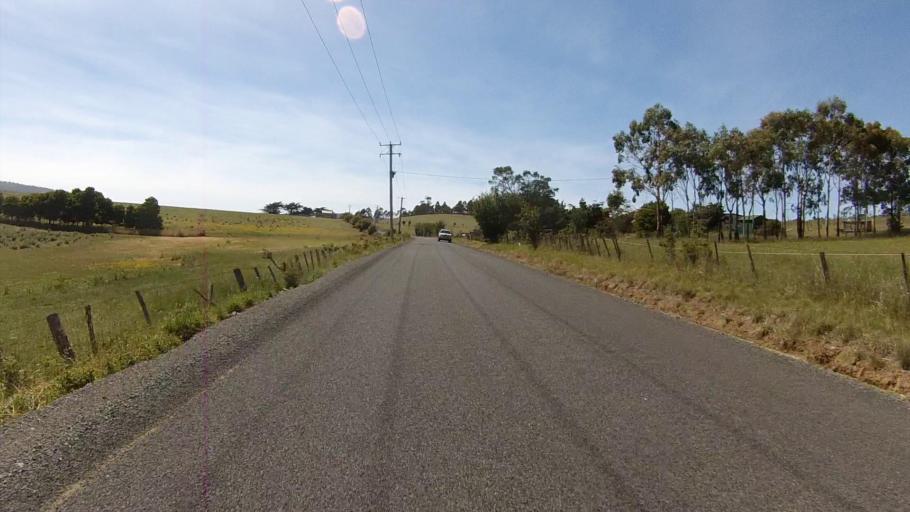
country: AU
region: Tasmania
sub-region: Sorell
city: Sorell
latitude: -42.7635
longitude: 147.6303
